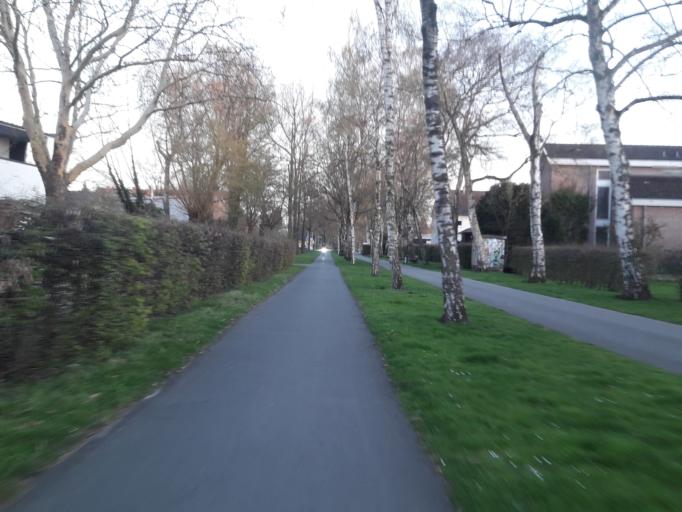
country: DE
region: North Rhine-Westphalia
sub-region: Regierungsbezirk Detmold
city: Paderborn
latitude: 51.7275
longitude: 8.7467
